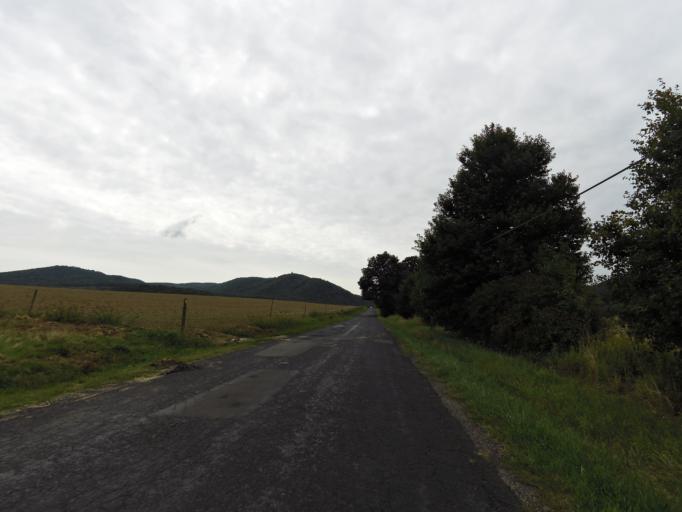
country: HU
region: Zala
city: Gyenesdias
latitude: 46.8528
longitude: 17.3026
